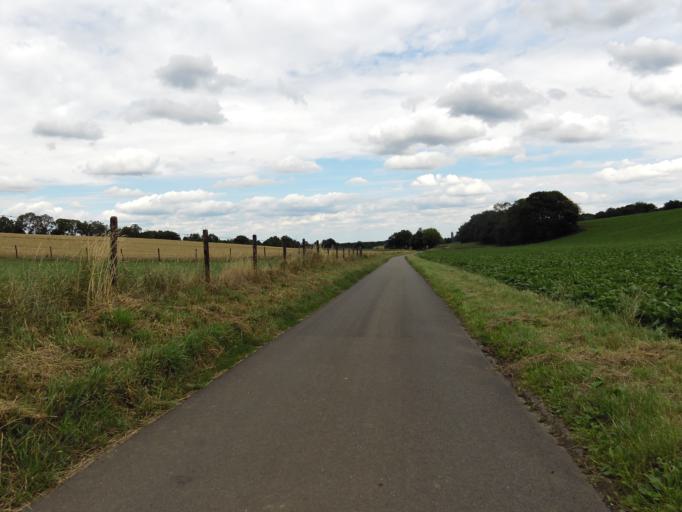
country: NL
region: Limburg
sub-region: Gemeente Schinnen
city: Doenrade
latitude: 50.9648
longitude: 5.9156
